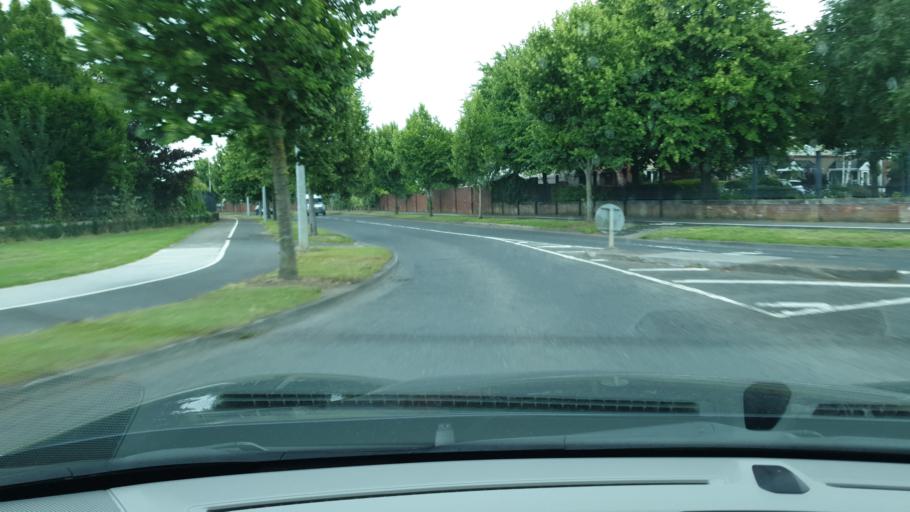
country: IE
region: Leinster
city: Lucan
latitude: 53.3426
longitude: -6.4466
